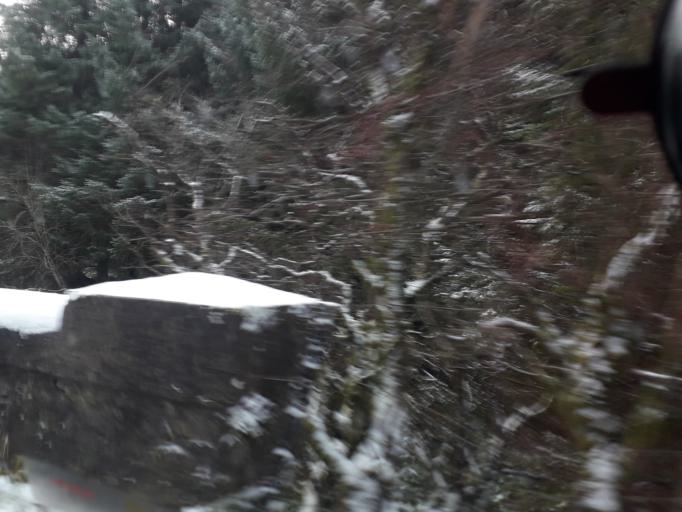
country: IE
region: Leinster
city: Ballyboden
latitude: 53.2391
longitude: -6.3197
